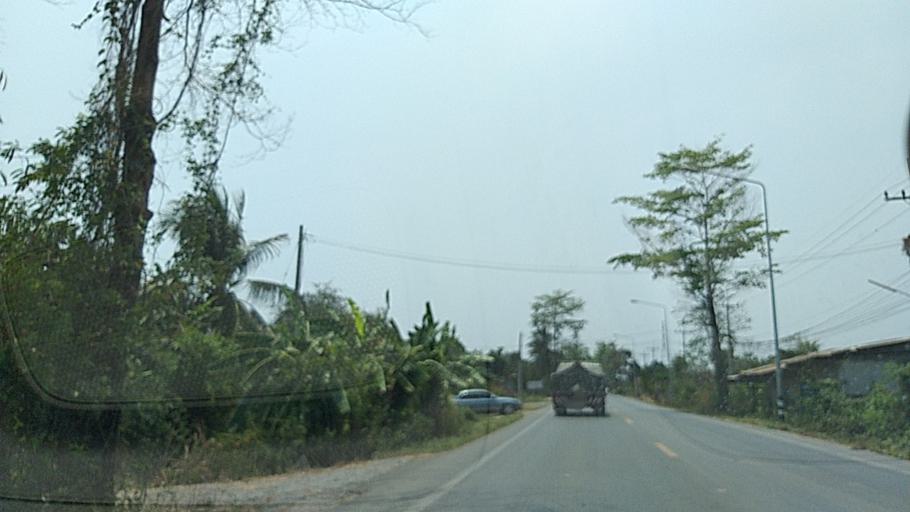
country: TH
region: Chachoengsao
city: Bang Nam Priao
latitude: 13.9140
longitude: 100.9743
